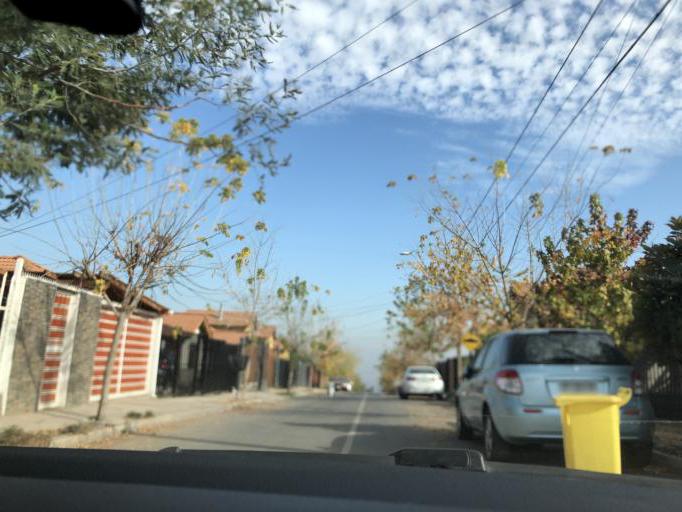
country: CL
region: Santiago Metropolitan
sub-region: Provincia de Cordillera
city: Puente Alto
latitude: -33.5878
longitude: -70.5314
